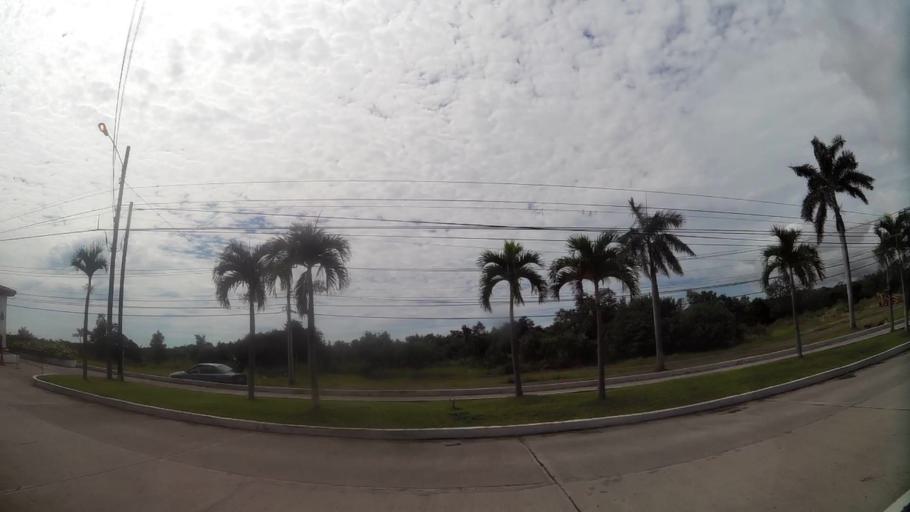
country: PA
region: Panama
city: Nueva Gorgona
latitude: 8.5374
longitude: -79.9054
